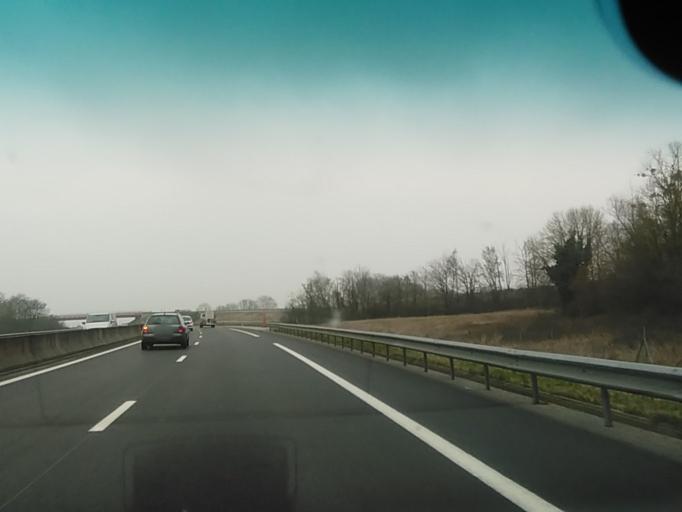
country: FR
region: Lower Normandy
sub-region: Departement de l'Orne
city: Gace
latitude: 48.7405
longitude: 0.2685
